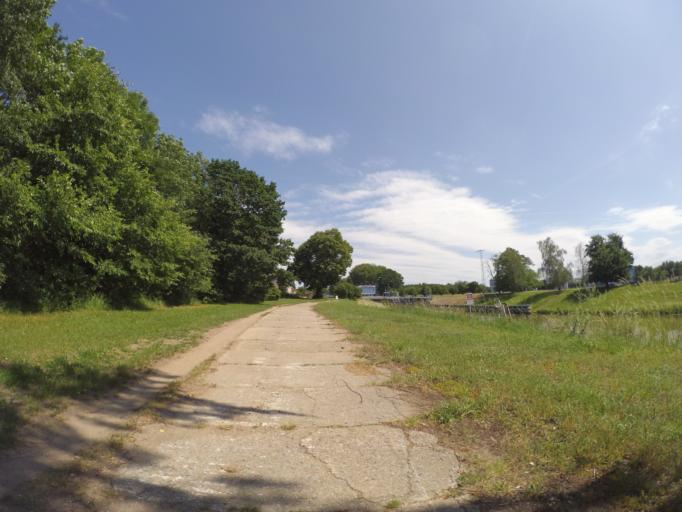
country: CZ
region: Central Bohemia
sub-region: Okres Nymburk
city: Sadska
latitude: 50.1708
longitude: 14.9394
